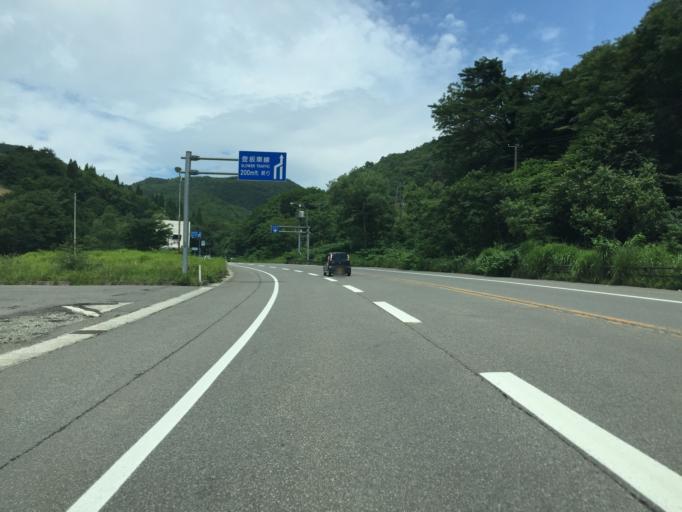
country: JP
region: Yamagata
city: Yonezawa
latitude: 37.8271
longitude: 140.2675
